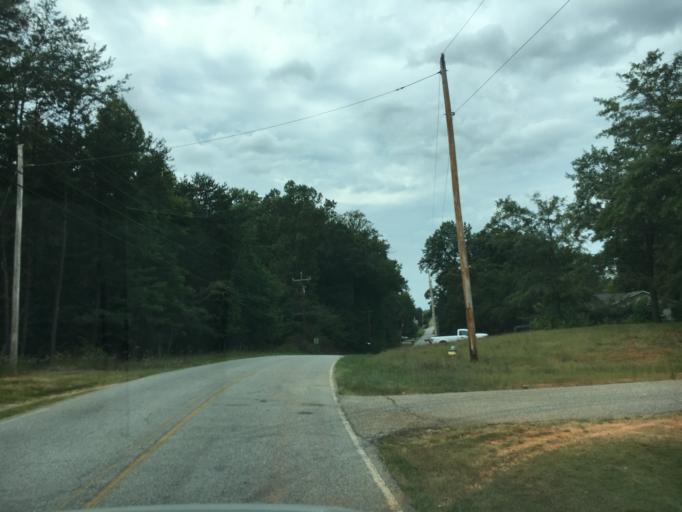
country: US
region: South Carolina
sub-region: Greenville County
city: Greer
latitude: 34.9291
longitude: -82.2126
